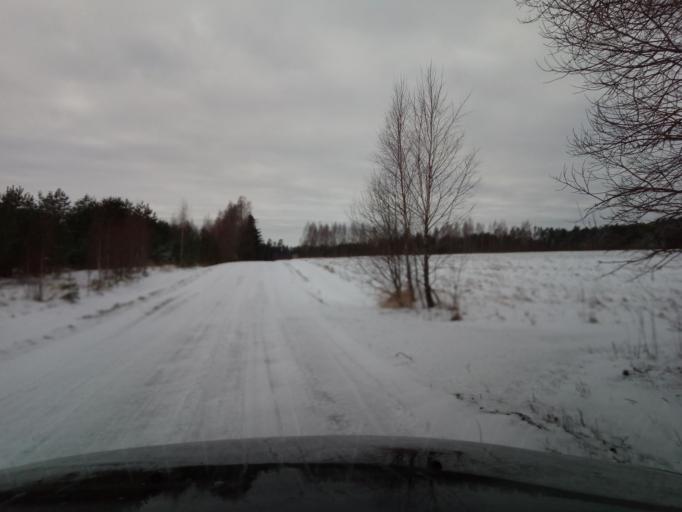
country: LT
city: Zarasai
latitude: 55.6794
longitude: 26.0008
